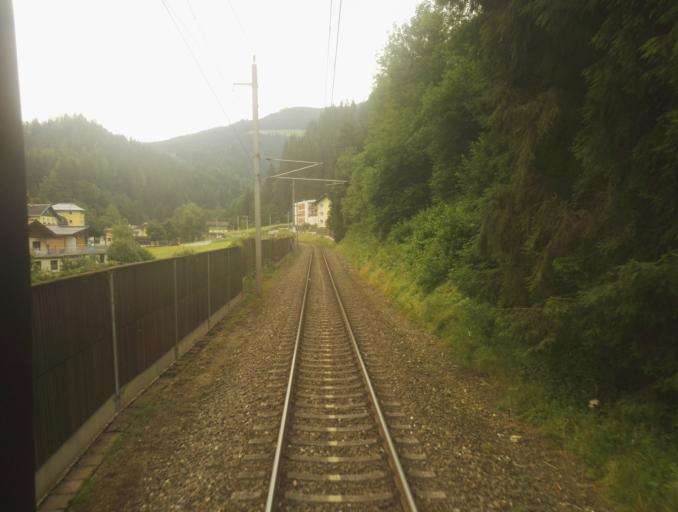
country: AT
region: Salzburg
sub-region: Politischer Bezirk Sankt Johann im Pongau
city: Huttau
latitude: 47.4150
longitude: 13.3077
